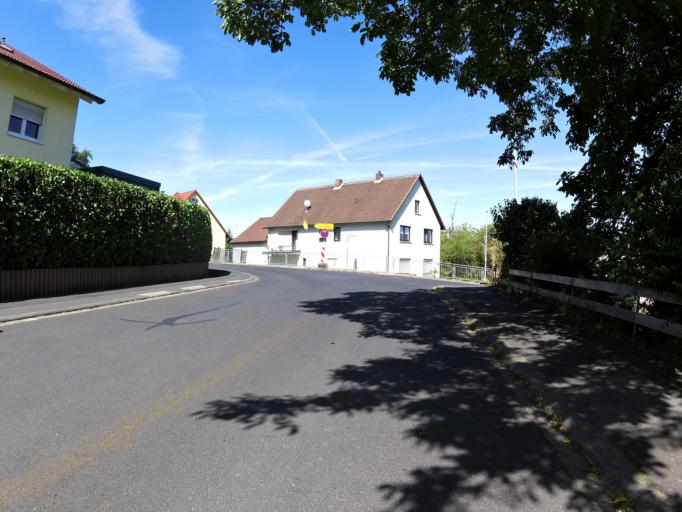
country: DE
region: Bavaria
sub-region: Regierungsbezirk Unterfranken
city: Guntersleben
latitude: 49.8682
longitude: 9.9015
